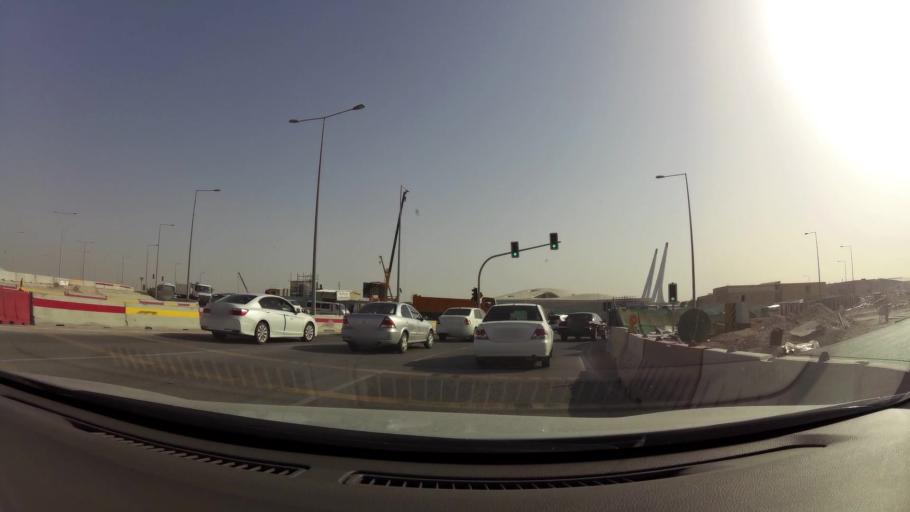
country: QA
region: Baladiyat ar Rayyan
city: Ar Rayyan
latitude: 25.3209
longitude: 51.4488
